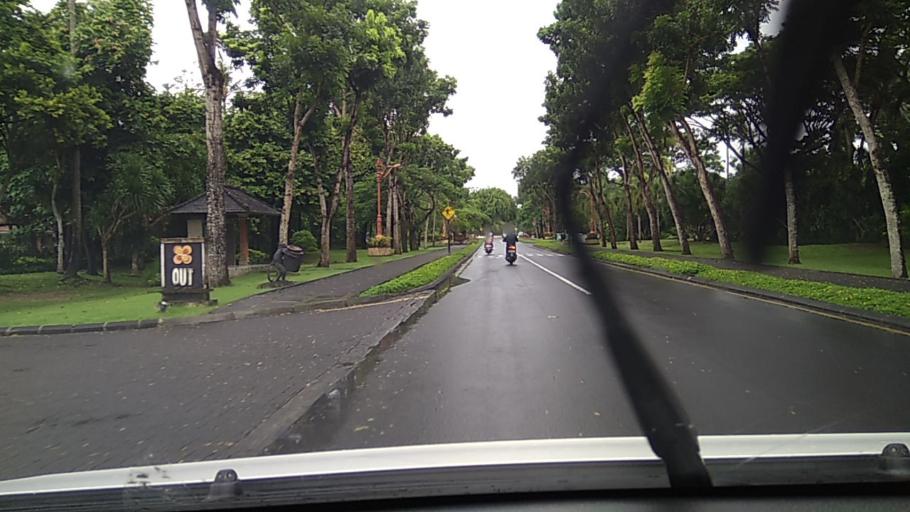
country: ID
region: Bali
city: Bualu
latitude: -8.8018
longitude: 115.2288
